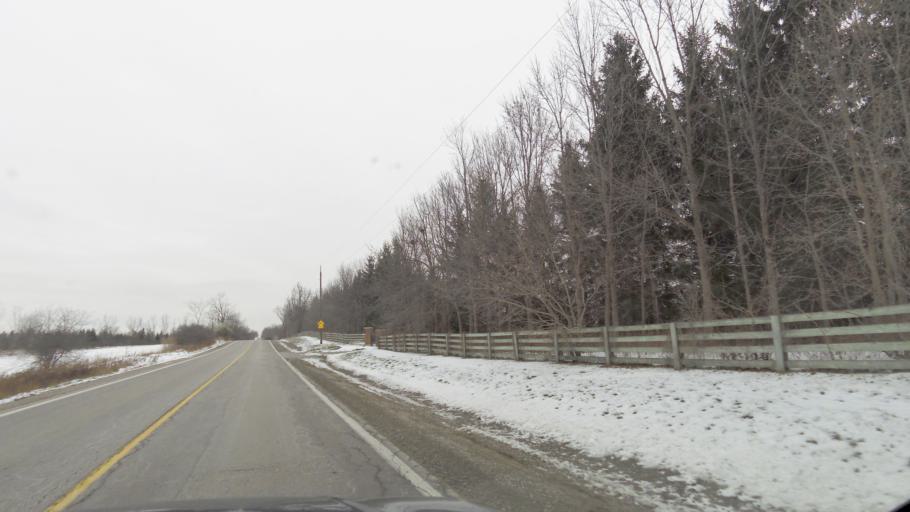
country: CA
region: Ontario
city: Vaughan
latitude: 43.8781
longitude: -79.5952
